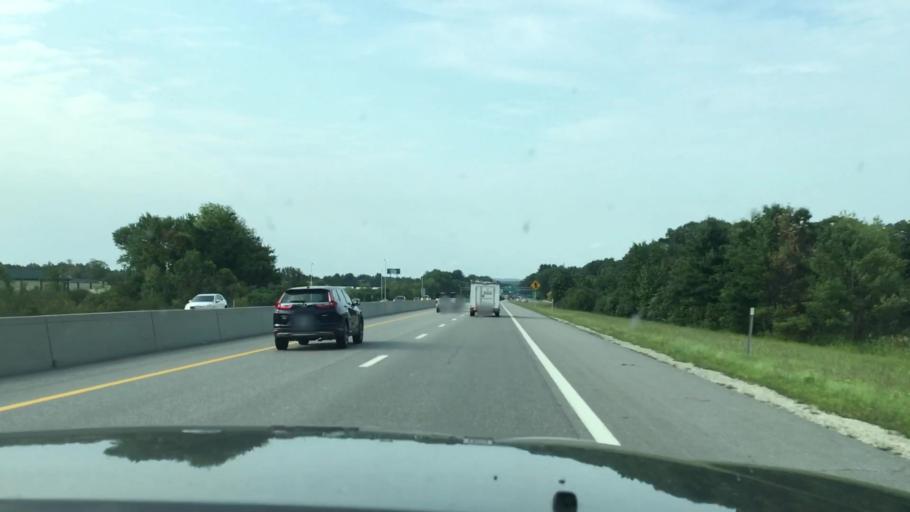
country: US
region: New Hampshire
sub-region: Hillsborough County
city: Bedford
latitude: 42.9517
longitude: -71.4723
